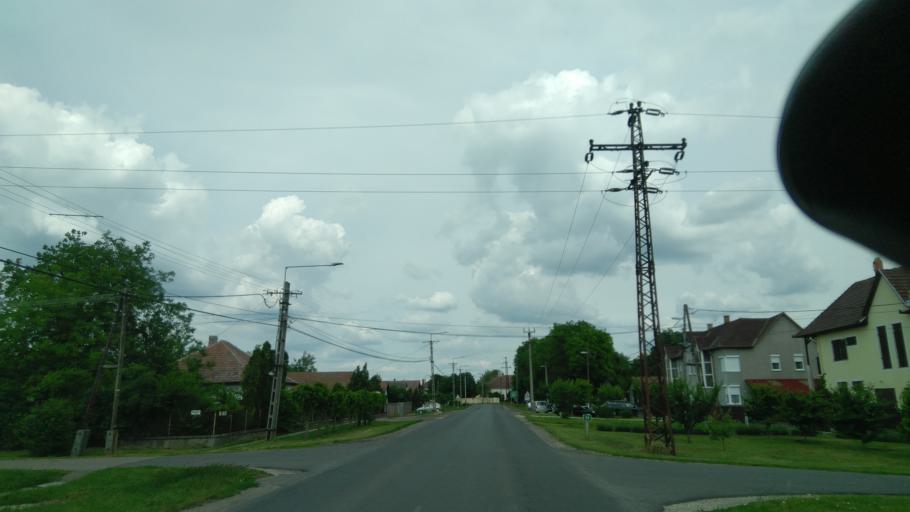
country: HU
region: Bekes
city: Mezohegyes
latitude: 46.3202
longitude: 20.8140
